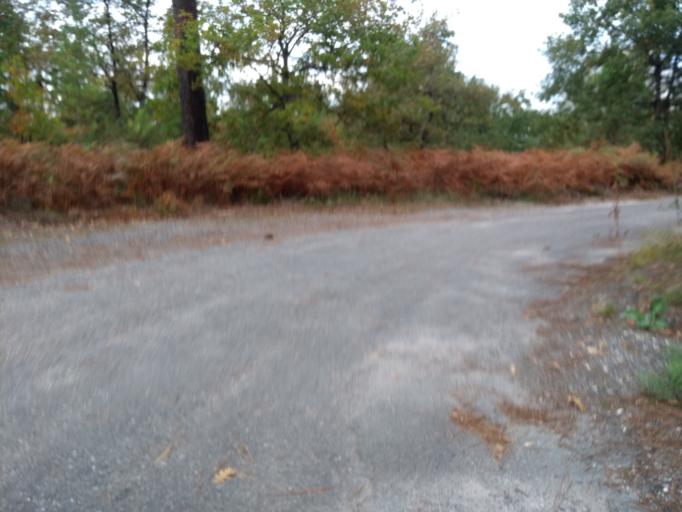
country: FR
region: Aquitaine
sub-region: Departement de la Gironde
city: Cestas
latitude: 44.7461
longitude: -0.6933
